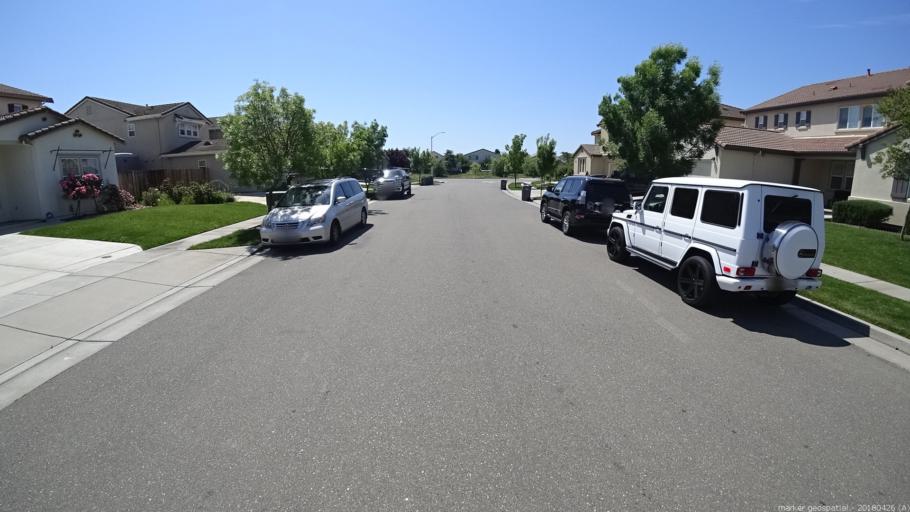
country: US
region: California
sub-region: Yolo County
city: West Sacramento
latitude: 38.5310
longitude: -121.5738
